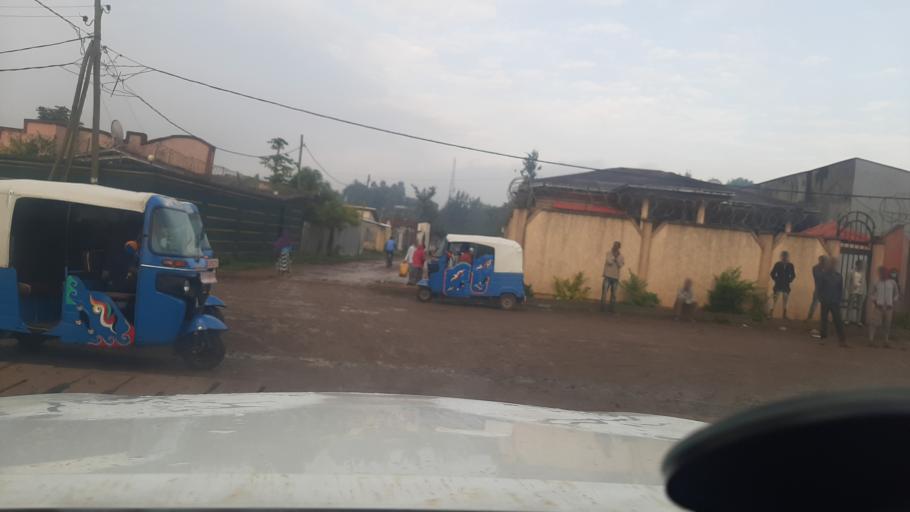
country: ET
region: Oromiya
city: Jima
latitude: 7.6751
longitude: 36.8456
